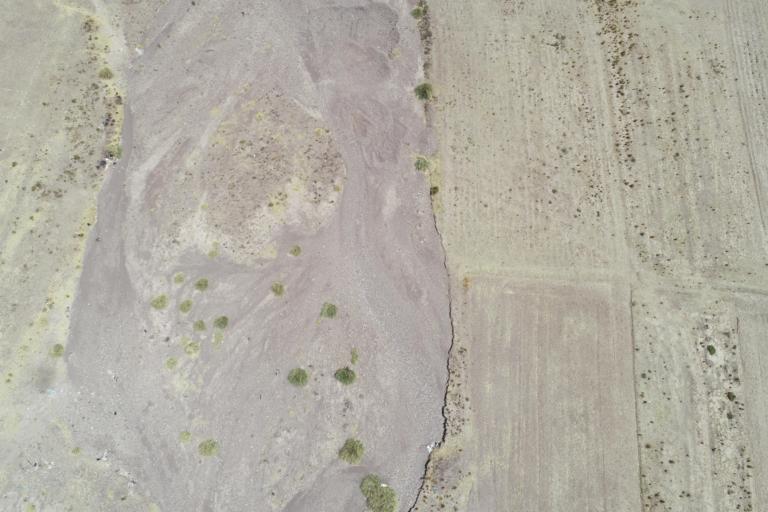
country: BO
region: La Paz
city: Achacachi
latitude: -15.9114
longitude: -68.8828
